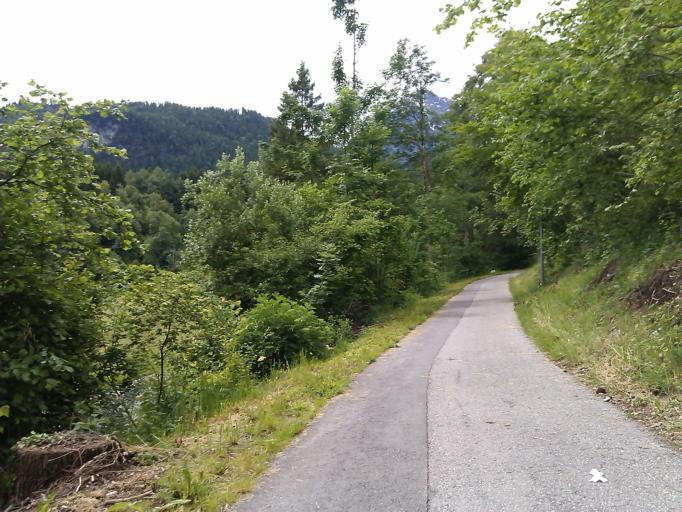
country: AT
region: Tyrol
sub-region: Politischer Bezirk Reutte
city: Reutte
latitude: 47.4758
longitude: 10.7234
